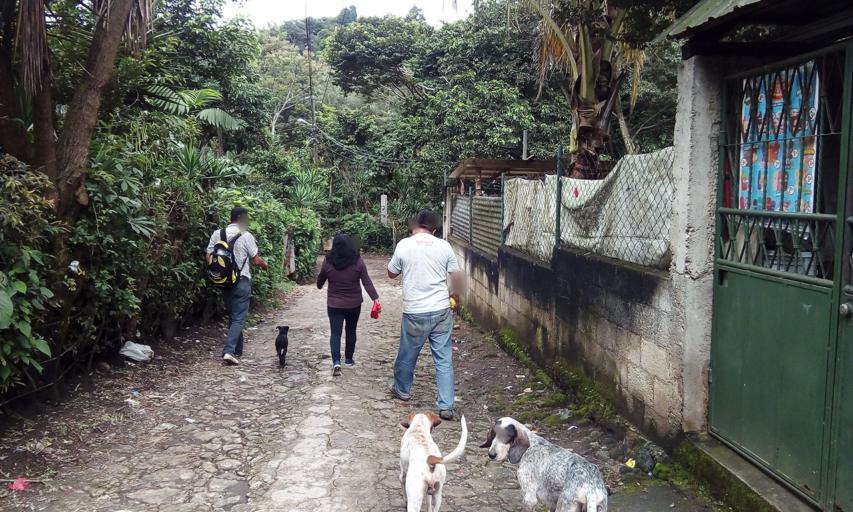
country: GT
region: Escuintla
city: San Vicente Pacaya
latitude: 14.3307
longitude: -90.6027
